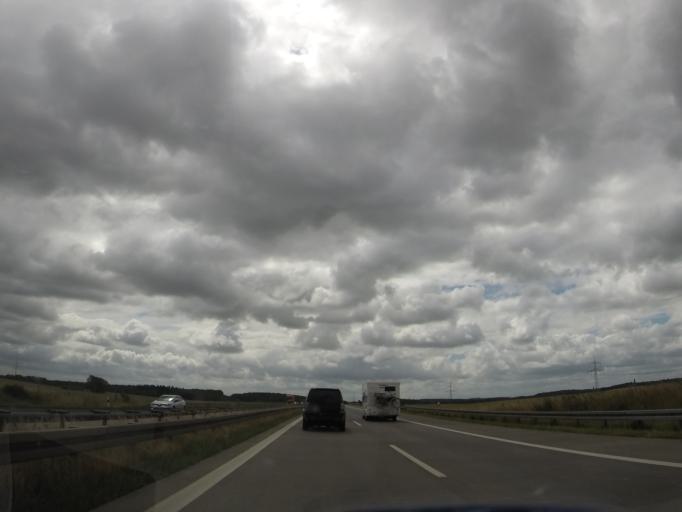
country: DE
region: Mecklenburg-Vorpommern
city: Kavelstorf
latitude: 53.9887
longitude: 12.1974
